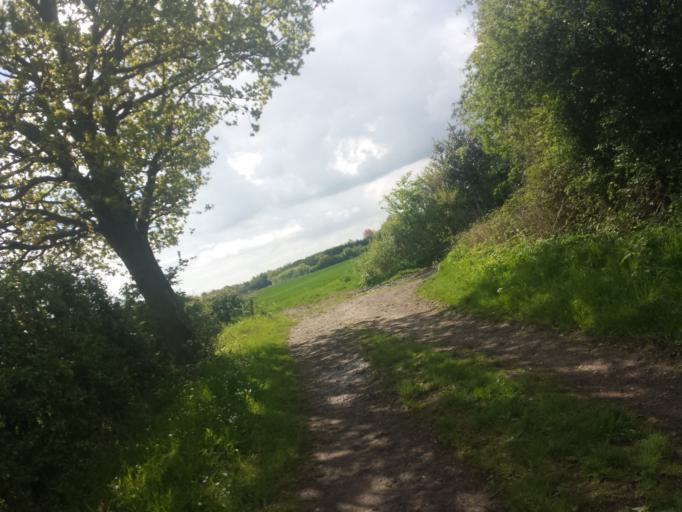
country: GB
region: England
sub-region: Essex
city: Great Bentley
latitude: 51.8791
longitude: 1.0457
